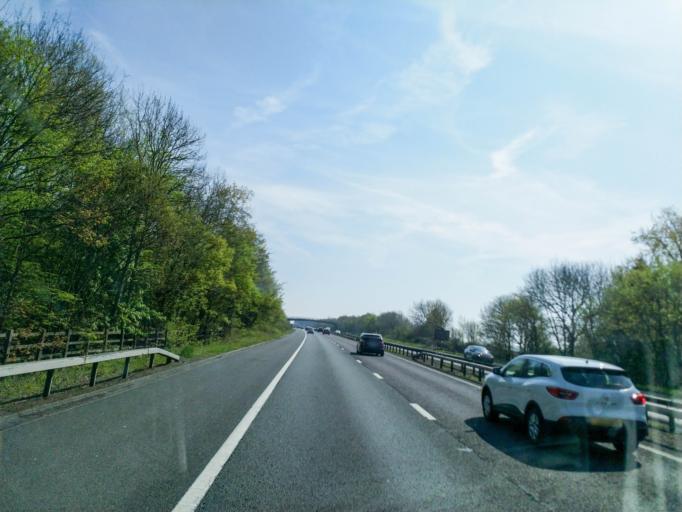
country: GB
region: England
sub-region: Kent
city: Kemsing
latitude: 51.3009
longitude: 0.2562
